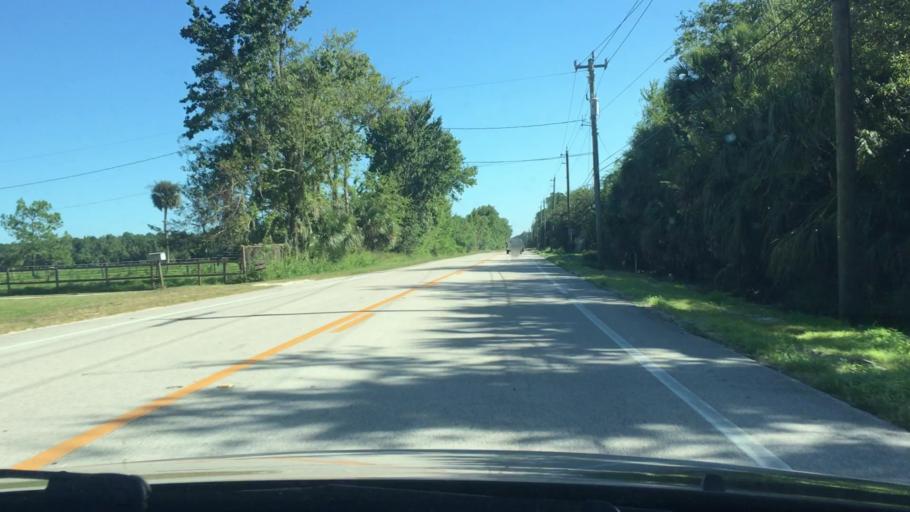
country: US
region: Florida
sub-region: Volusia County
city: South Daytona
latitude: 29.1417
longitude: -81.0783
